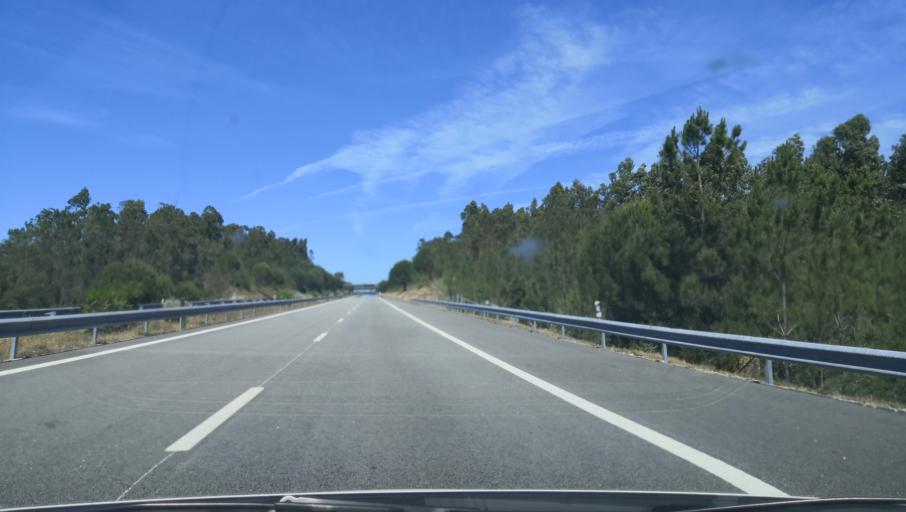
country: PT
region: Coimbra
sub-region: Montemor-O-Velho
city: Montemor-o-Velho
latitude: 40.2260
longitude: -8.6710
